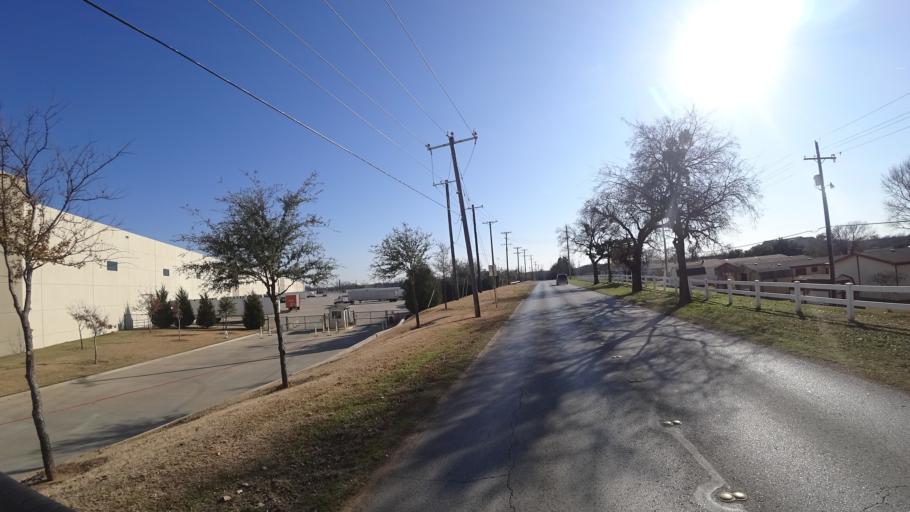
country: US
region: Texas
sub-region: Dallas County
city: Coppell
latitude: 32.9922
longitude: -97.0160
